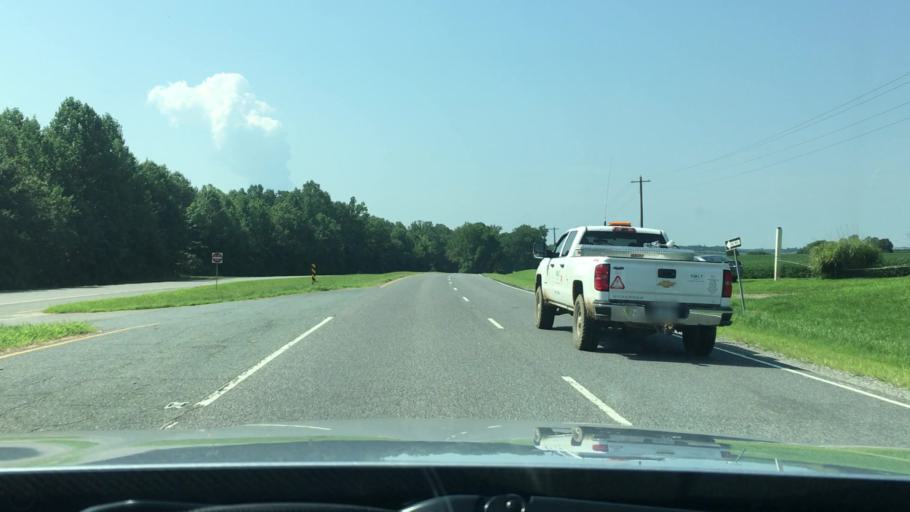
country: US
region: Virginia
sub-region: Caroline County
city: Bowling Green
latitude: 37.9859
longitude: -77.4190
